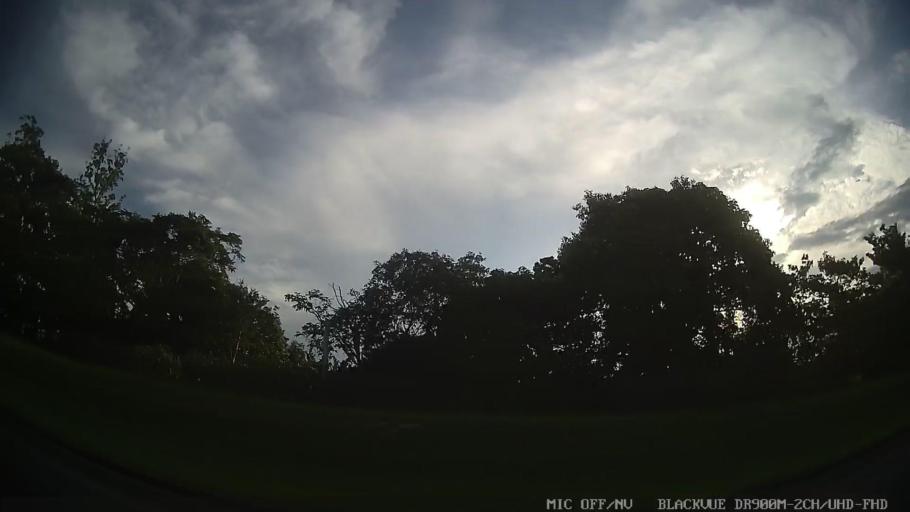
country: BR
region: Sao Paulo
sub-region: Tiete
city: Tiete
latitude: -23.1542
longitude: -47.6601
